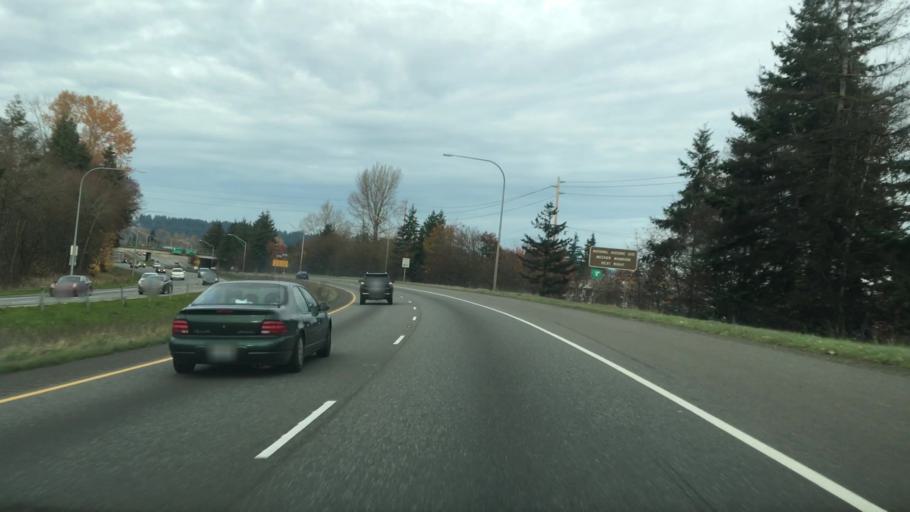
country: US
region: Washington
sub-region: Pierce County
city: Puyallup
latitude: 47.1827
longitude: -122.2835
